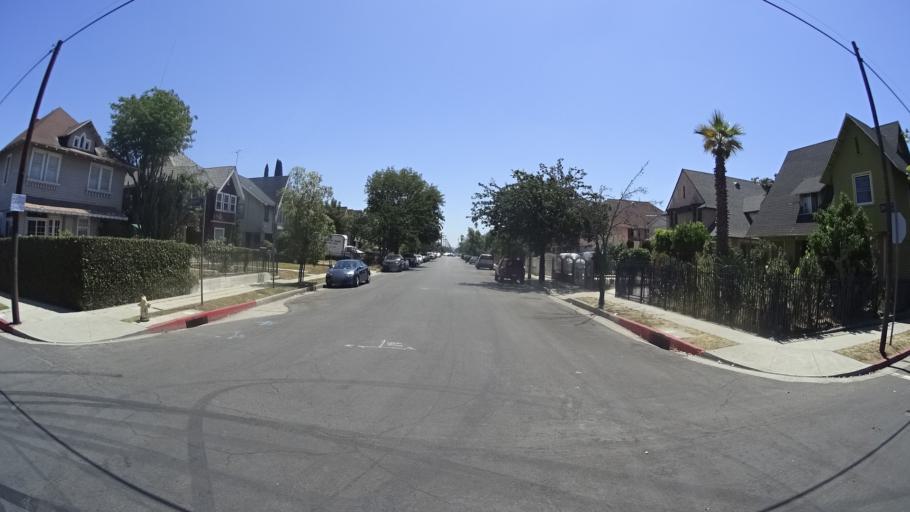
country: US
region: California
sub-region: Los Angeles County
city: View Park-Windsor Hills
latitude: 34.0345
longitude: -118.3025
